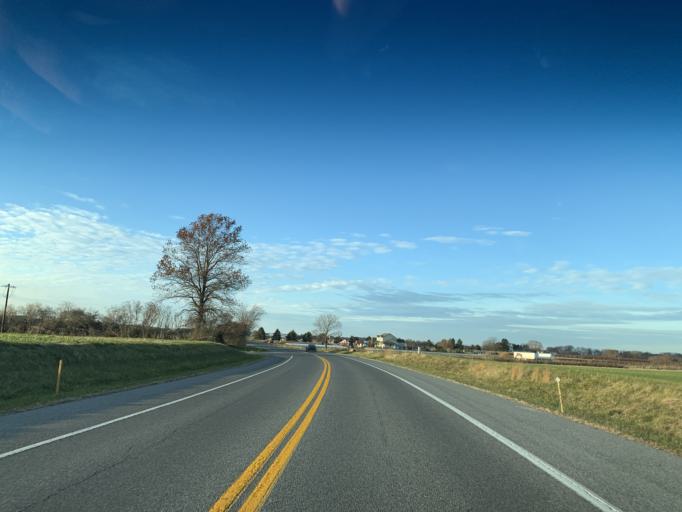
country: US
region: Maryland
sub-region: Kent County
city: Chestertown
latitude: 39.2515
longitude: -76.0768
